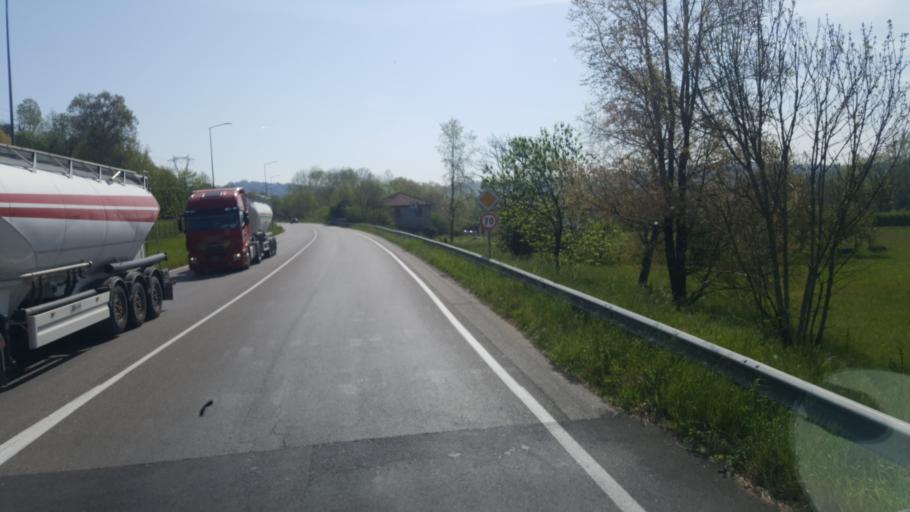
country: IT
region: Lombardy
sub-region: Provincia di Varese
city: Casciago
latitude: 45.8063
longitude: 8.7874
